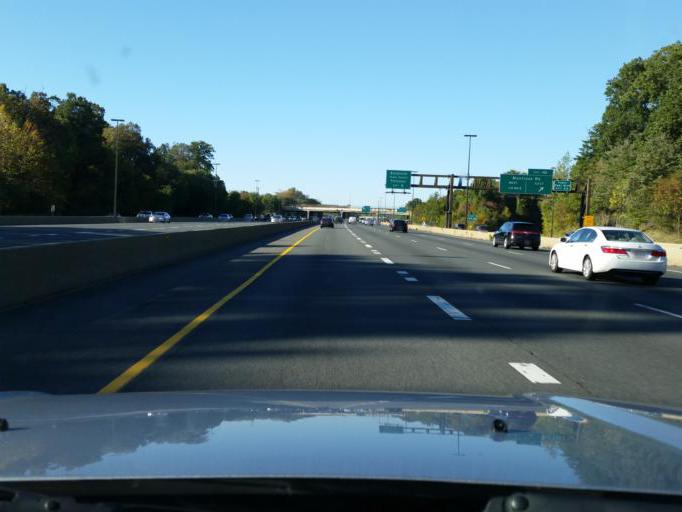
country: US
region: Maryland
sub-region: Montgomery County
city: Rockville
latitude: 39.0522
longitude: -77.1527
